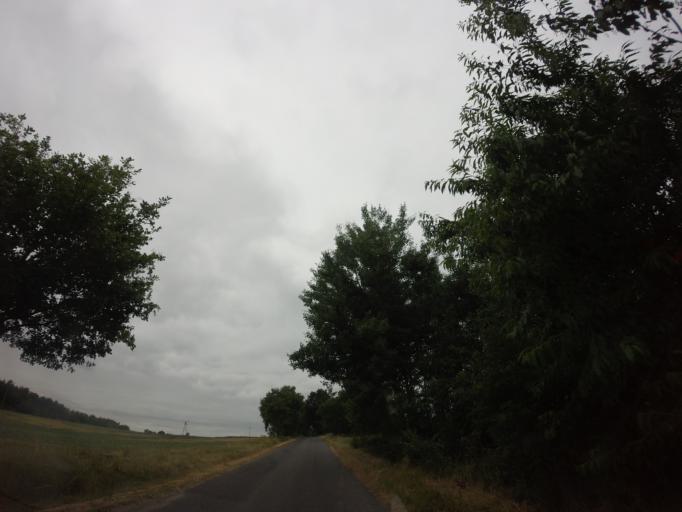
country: PL
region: West Pomeranian Voivodeship
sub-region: Powiat choszczenski
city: Bierzwnik
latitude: 53.1478
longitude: 15.6551
